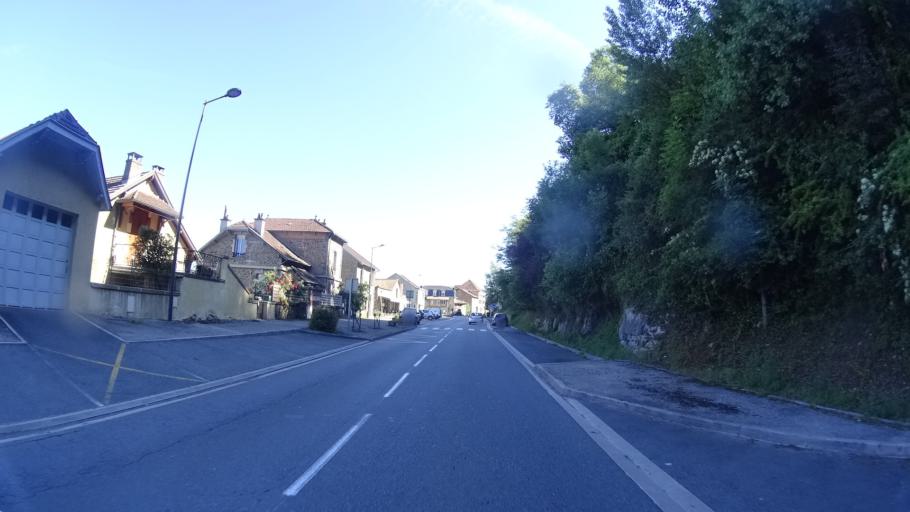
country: FR
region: Midi-Pyrenees
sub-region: Departement de l'Aveyron
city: Capdenac-Gare
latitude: 44.5791
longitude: 2.0721
